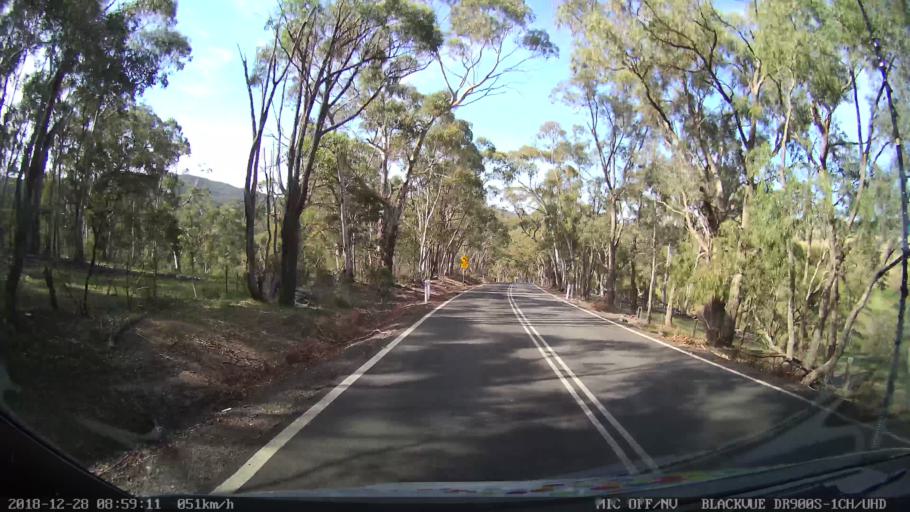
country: AU
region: New South Wales
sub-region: Upper Lachlan Shire
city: Crookwell
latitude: -34.1323
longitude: 149.3322
